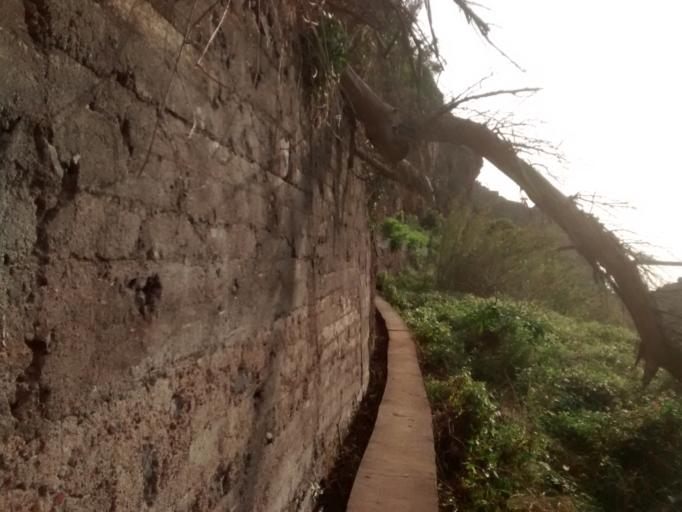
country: PT
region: Madeira
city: Camara de Lobos
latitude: 32.6604
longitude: -16.9601
